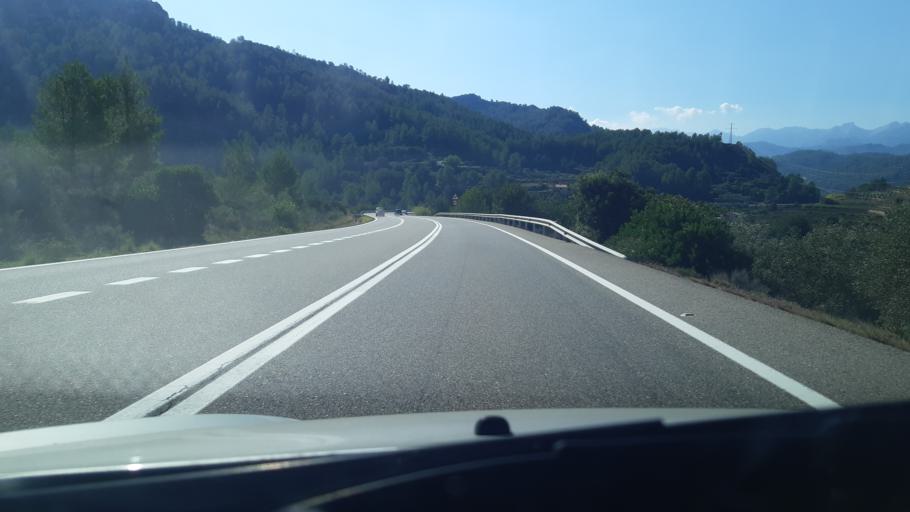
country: ES
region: Catalonia
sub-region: Provincia de Tarragona
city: Benifallet
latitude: 40.9846
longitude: 0.5368
